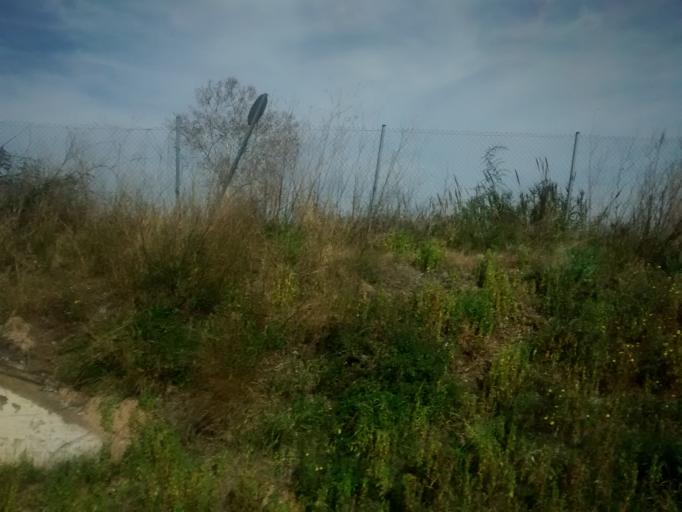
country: ES
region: Catalonia
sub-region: Provincia de Barcelona
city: Sant Boi de Llobregat
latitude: 41.3515
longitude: 2.0376
